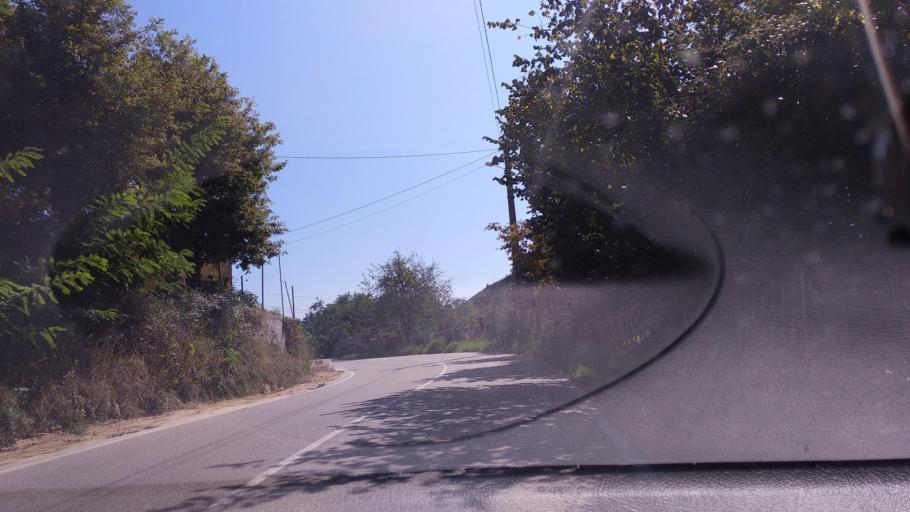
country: ES
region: Galicia
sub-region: Provincia de Pontevedra
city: Moana
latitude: 42.2838
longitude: -8.7515
